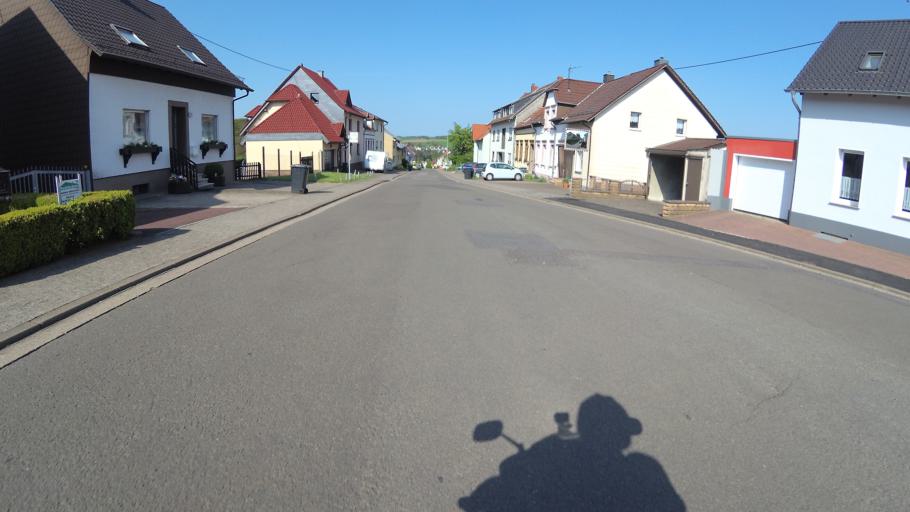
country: DE
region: Saarland
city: Illingen
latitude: 49.3678
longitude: 7.0461
